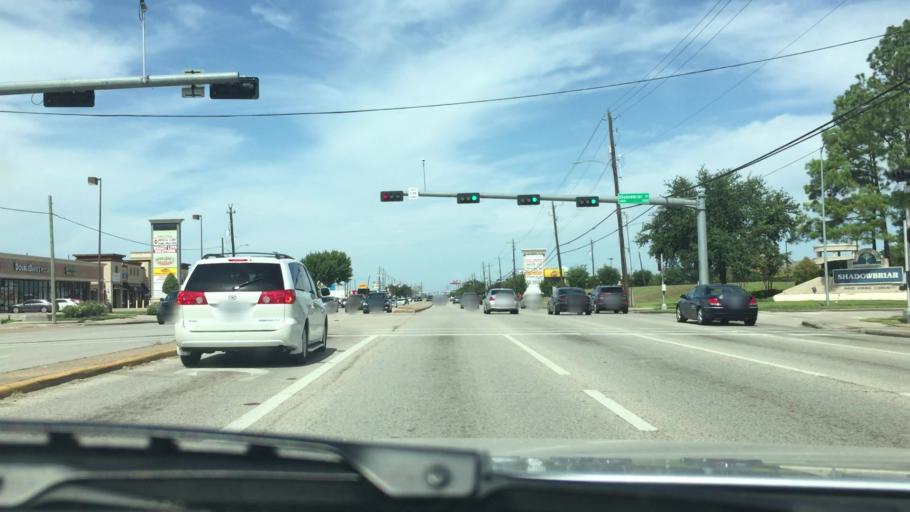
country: US
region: Texas
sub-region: Harris County
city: Bunker Hill Village
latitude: 29.7363
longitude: -95.5978
